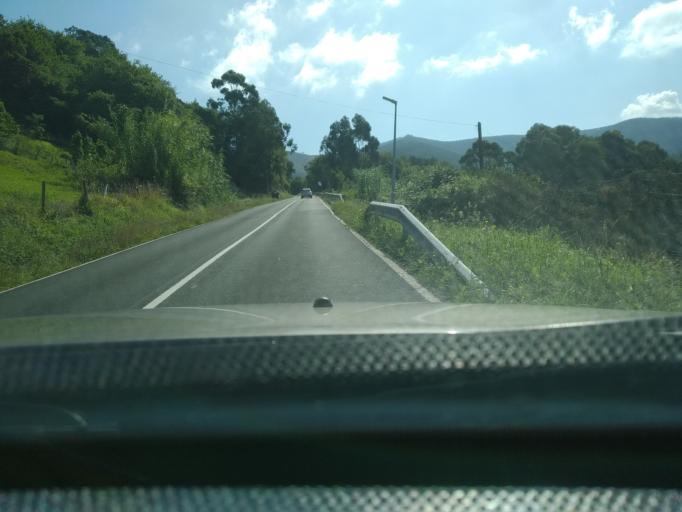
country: ES
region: Basque Country
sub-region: Bizkaia
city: Bakio
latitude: 43.4334
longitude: -2.7904
